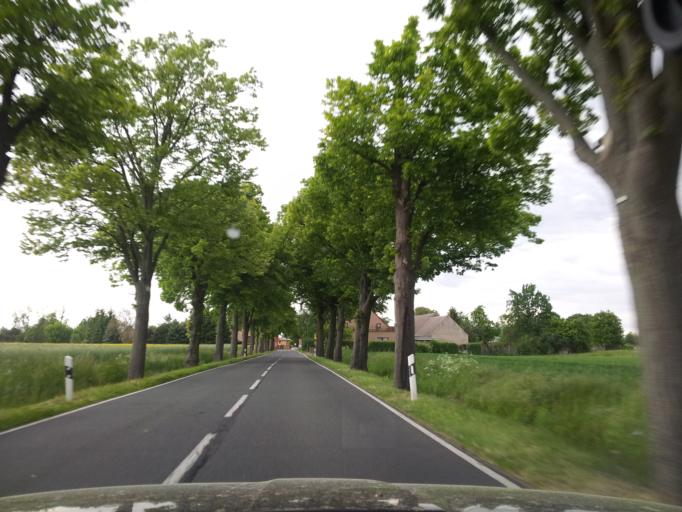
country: DE
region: Brandenburg
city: Niedergorsdorf
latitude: 51.9827
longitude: 12.9499
